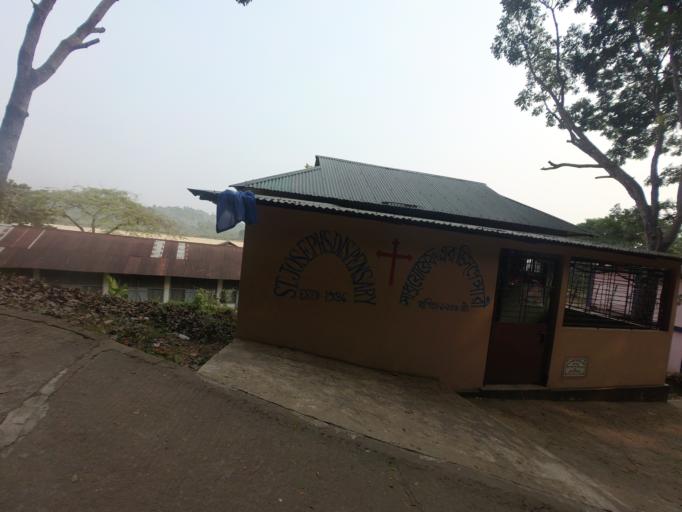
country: BD
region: Dhaka
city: Netrakona
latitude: 25.1717
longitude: 90.6589
